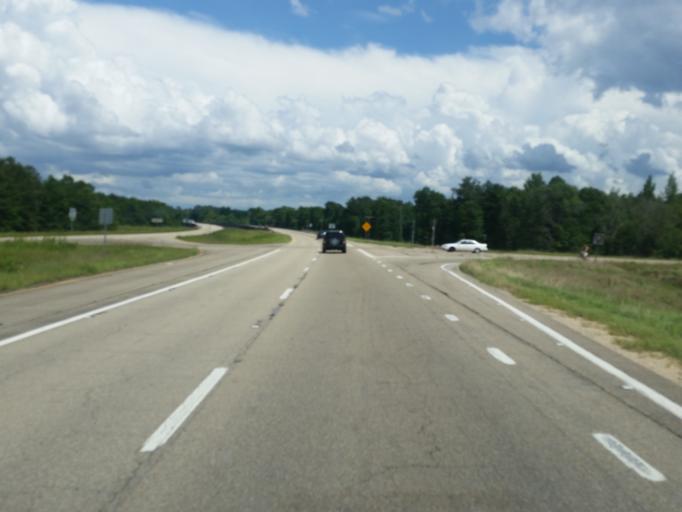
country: US
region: Mississippi
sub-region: Perry County
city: New Augusta
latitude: 31.1097
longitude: -88.8148
